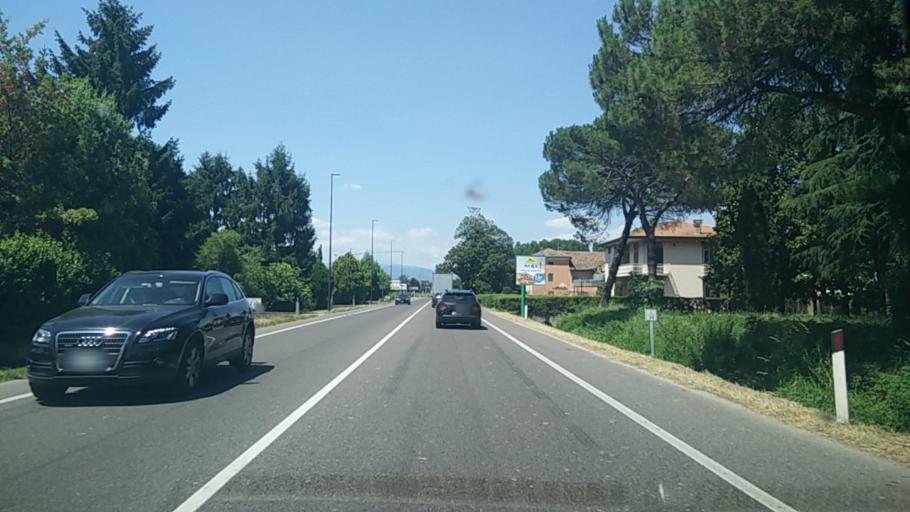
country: IT
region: Veneto
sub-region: Provincia di Padova
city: San Giorgio in Bosco
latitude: 45.5954
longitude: 11.8048
